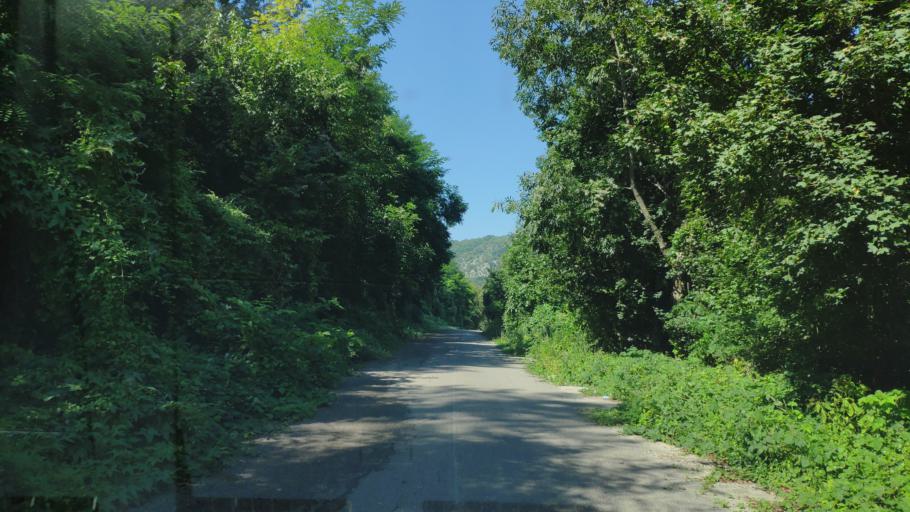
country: SK
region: Kosicky
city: Roznava
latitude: 48.5477
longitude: 20.4139
